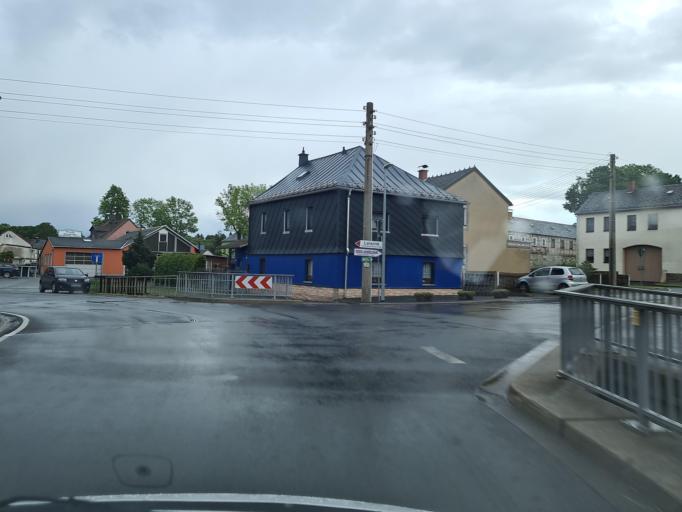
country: DE
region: Saxony
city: Muhltroff
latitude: 50.5012
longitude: 11.9109
